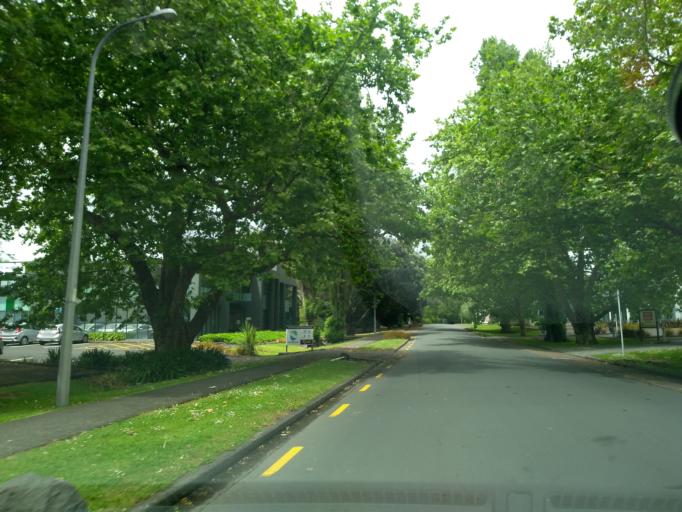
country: NZ
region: Auckland
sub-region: Auckland
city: Tamaki
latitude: -36.9210
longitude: 174.8210
